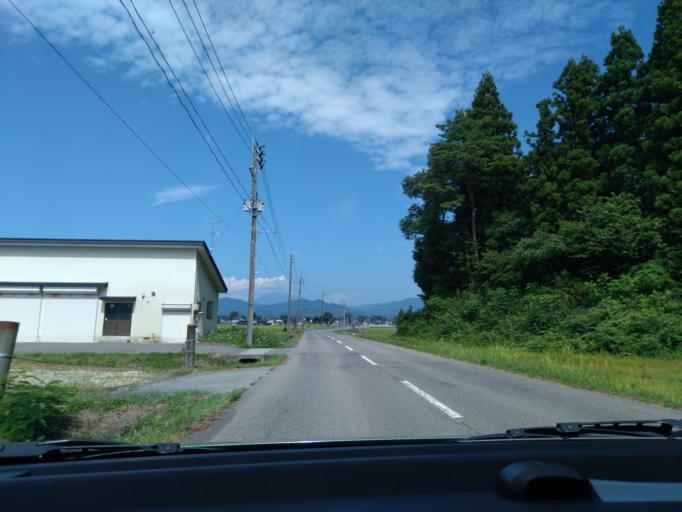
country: JP
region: Akita
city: Kakunodatemachi
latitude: 39.6009
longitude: 140.5823
